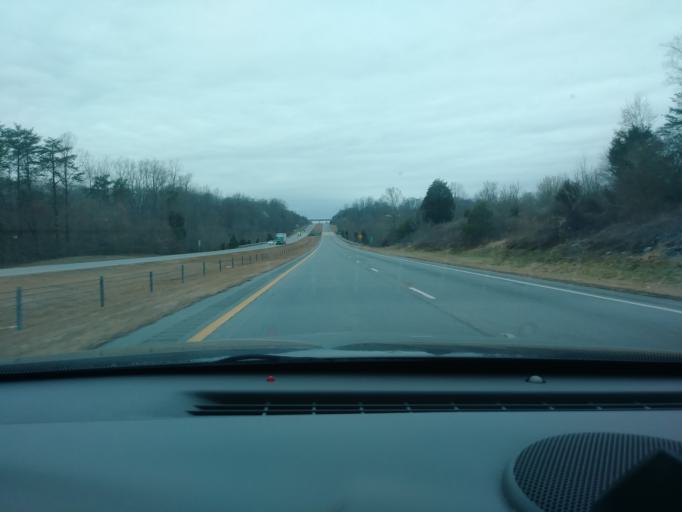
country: US
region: North Carolina
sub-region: Yadkin County
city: Yadkinville
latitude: 36.1187
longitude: -80.7176
